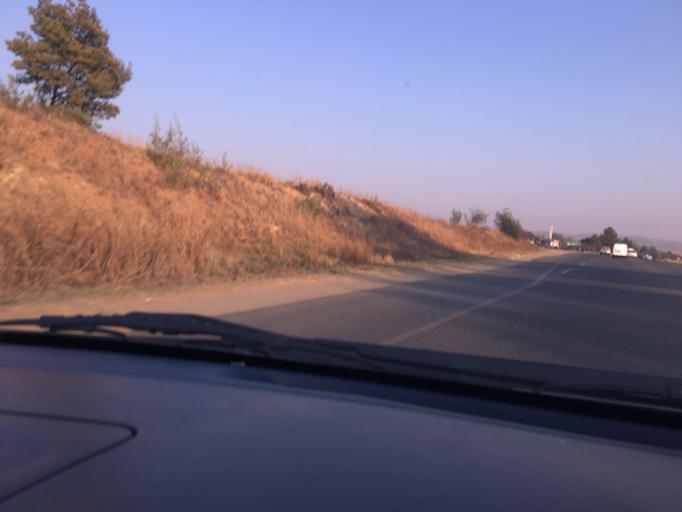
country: ZA
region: Gauteng
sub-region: West Rand District Municipality
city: Muldersdriseloop
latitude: -26.0272
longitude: 27.8668
